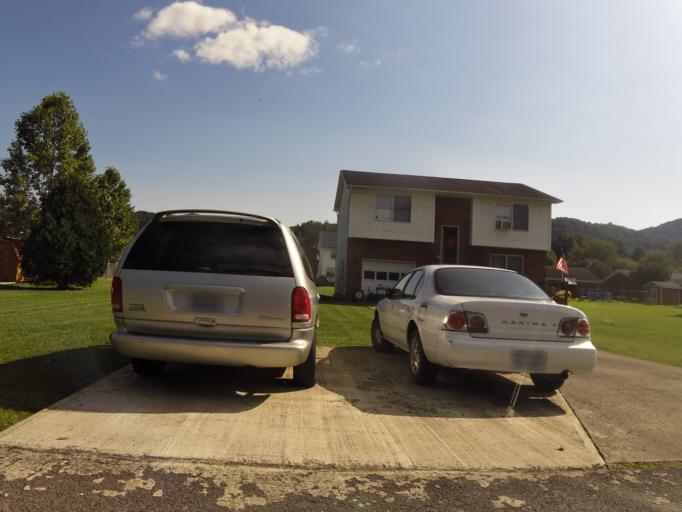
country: US
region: Kentucky
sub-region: Bell County
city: Middlesboro
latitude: 36.6017
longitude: -83.7284
